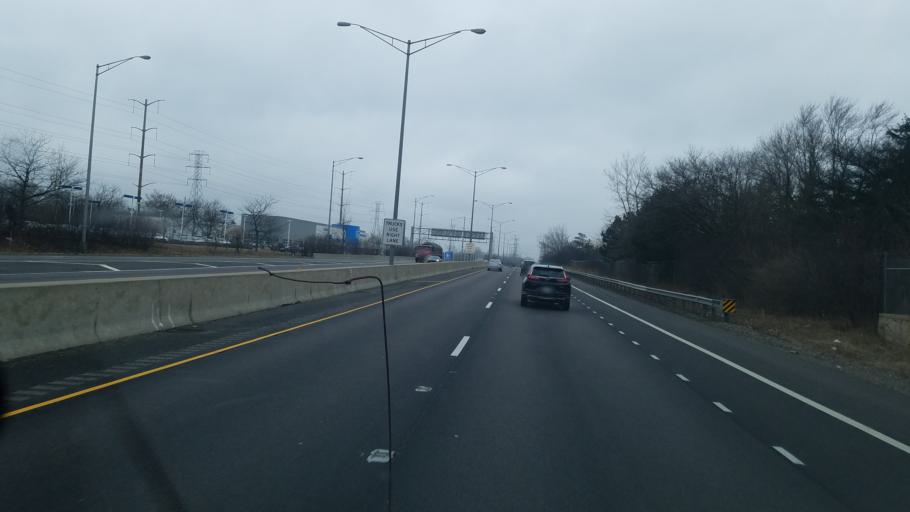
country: US
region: Illinois
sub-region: Lake County
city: Highland Park
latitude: 42.1606
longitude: -87.8065
